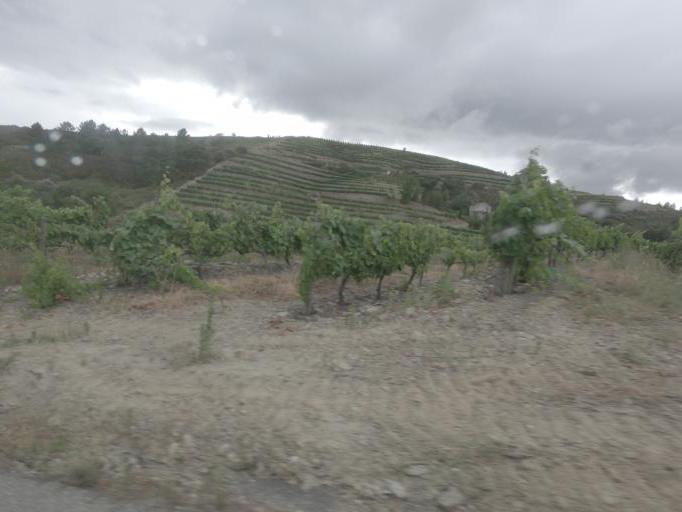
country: PT
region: Vila Real
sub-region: Sabrosa
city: Sabrosa
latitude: 41.2366
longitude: -7.4947
